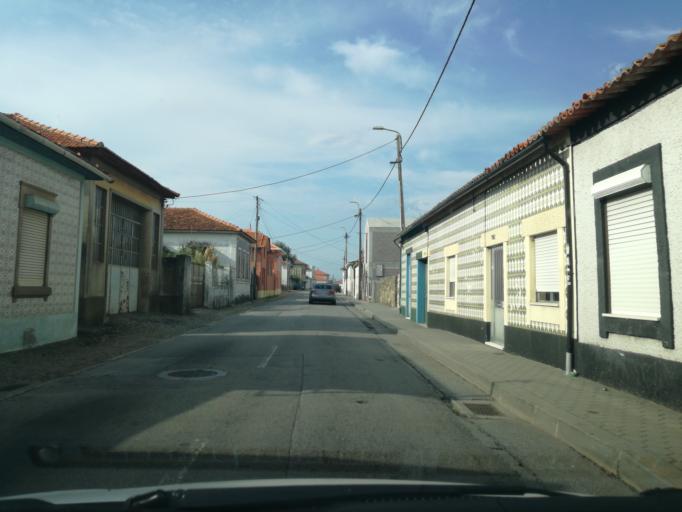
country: PT
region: Porto
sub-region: Vila Nova de Gaia
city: Azenha
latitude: 41.0726
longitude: -8.6253
